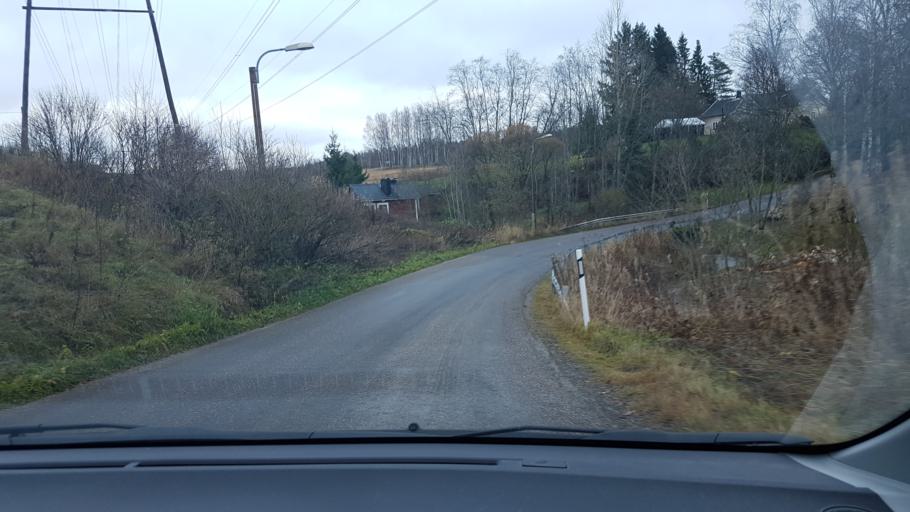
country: FI
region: Uusimaa
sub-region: Helsinki
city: Vantaa
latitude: 60.2829
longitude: 25.1396
